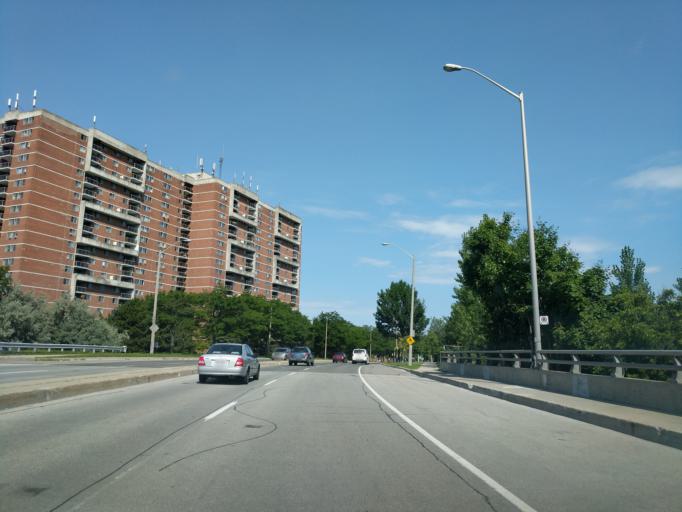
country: CA
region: Ontario
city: Scarborough
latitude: 43.8106
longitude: -79.2244
